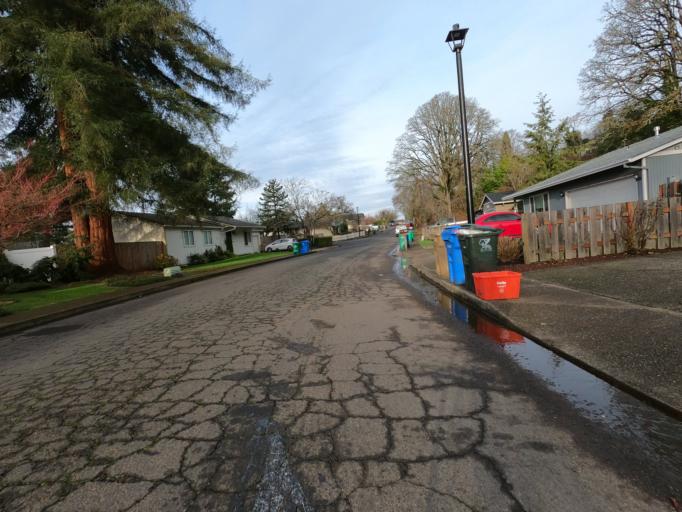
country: US
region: Oregon
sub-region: Clackamas County
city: Jennings Lodge
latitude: 45.3943
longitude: -122.6011
